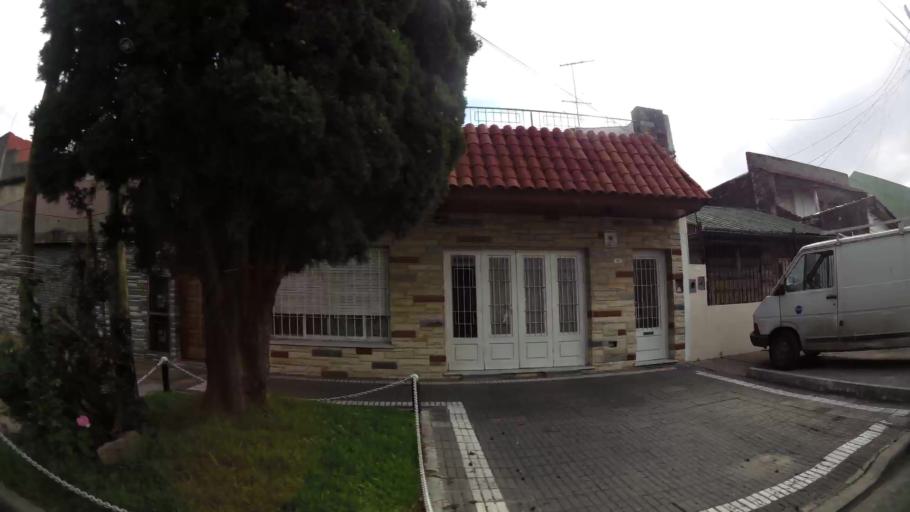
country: AR
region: Buenos Aires
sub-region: Partido de Lanus
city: Lanus
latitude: -34.6922
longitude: -58.3807
